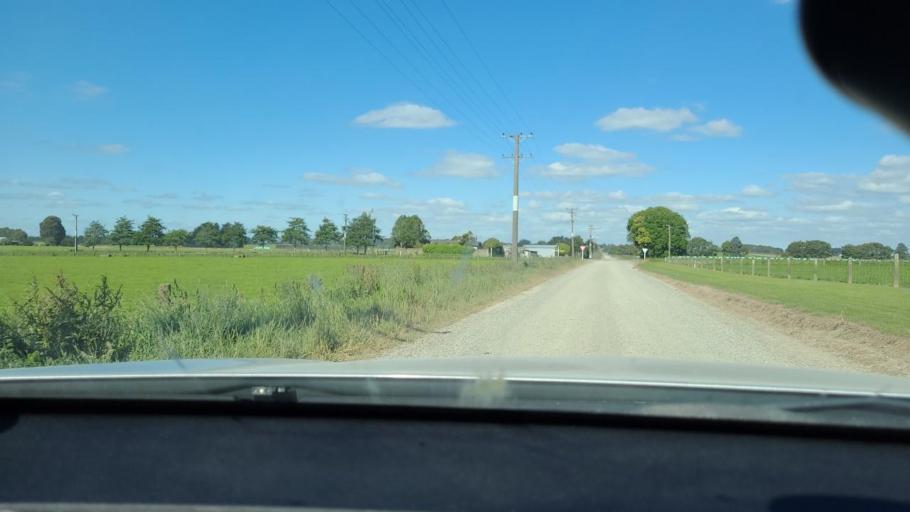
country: NZ
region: Southland
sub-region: Southland District
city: Riverton
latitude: -46.2712
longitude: 168.1772
